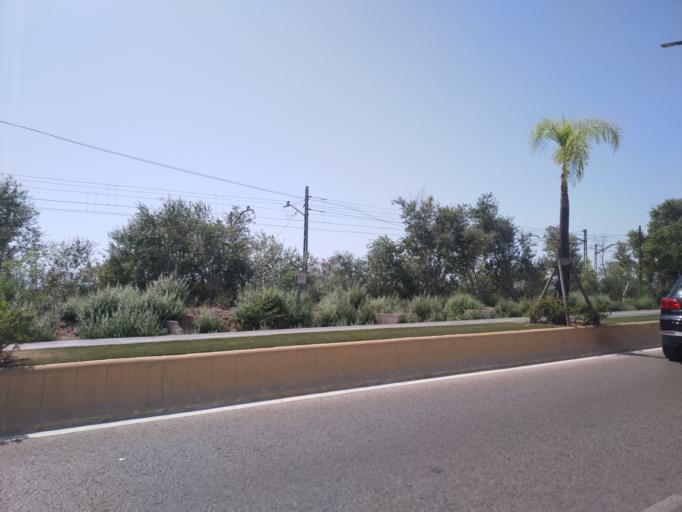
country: ES
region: Andalusia
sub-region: Provincia de Cadiz
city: Chiclana de la Frontera
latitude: 36.4372
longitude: -6.1441
